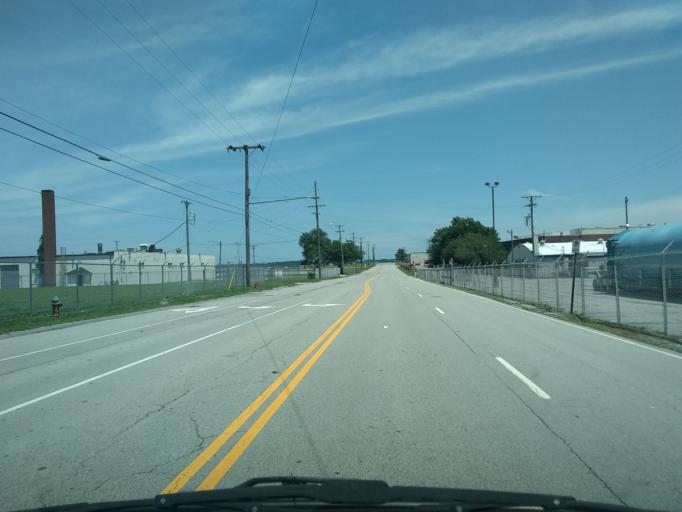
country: US
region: Tennessee
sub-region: Davidson County
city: Oak Hill
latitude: 36.1242
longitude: -86.6959
